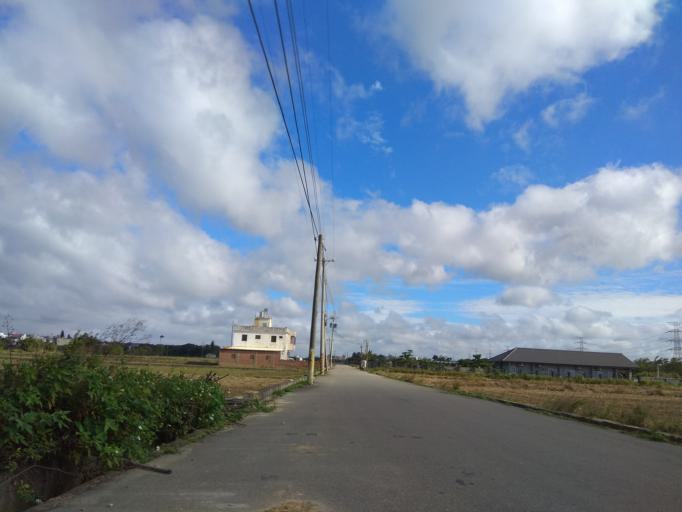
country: TW
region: Taiwan
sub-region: Hsinchu
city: Zhubei
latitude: 24.9728
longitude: 121.0757
